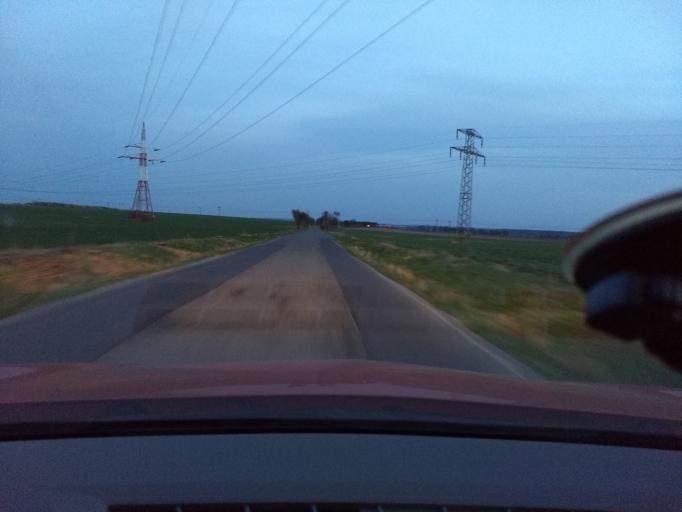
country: CZ
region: Central Bohemia
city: Jenec
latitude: 50.0619
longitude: 14.1866
